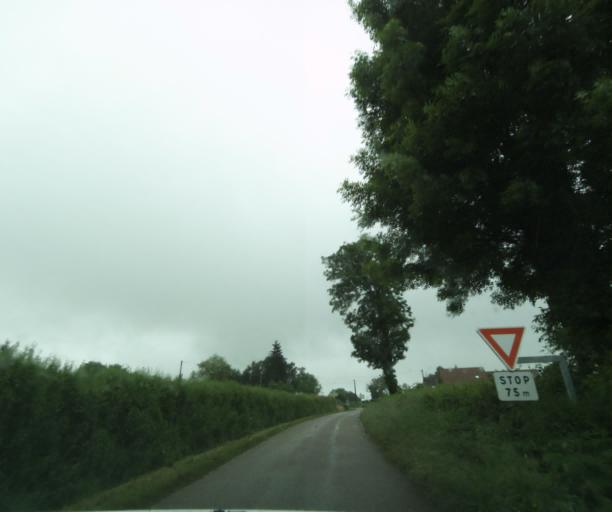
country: FR
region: Bourgogne
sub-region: Departement de Saone-et-Loire
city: Charolles
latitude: 46.3618
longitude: 4.2164
